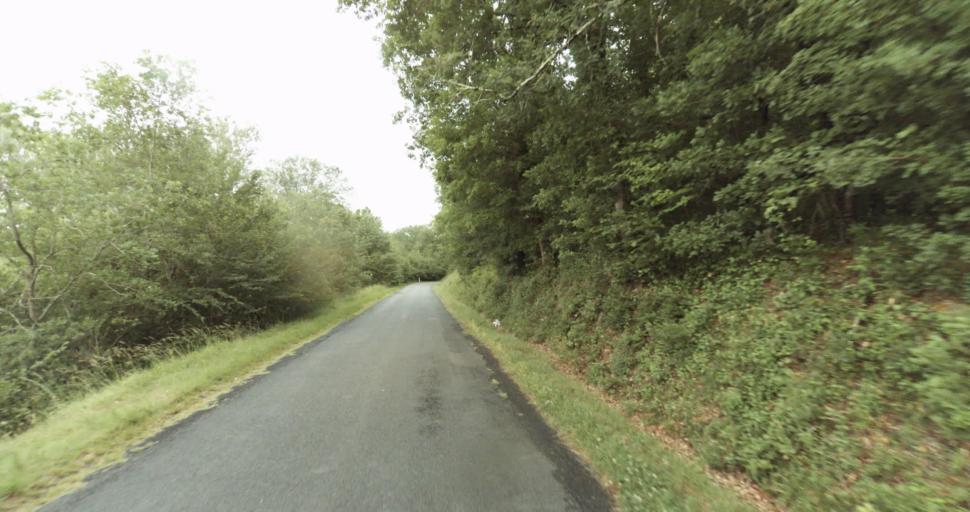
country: FR
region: Aquitaine
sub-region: Departement de la Dordogne
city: Beaumont-du-Perigord
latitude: 44.7536
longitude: 0.8196
